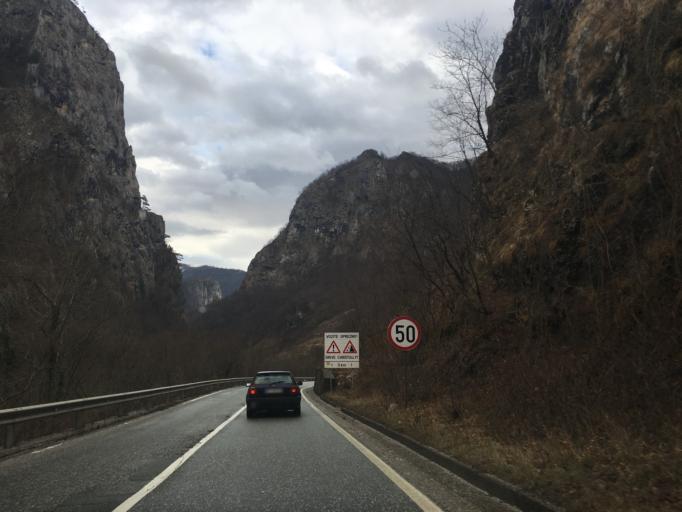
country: RS
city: Sokolovo Brdo
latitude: 43.1652
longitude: 19.7694
